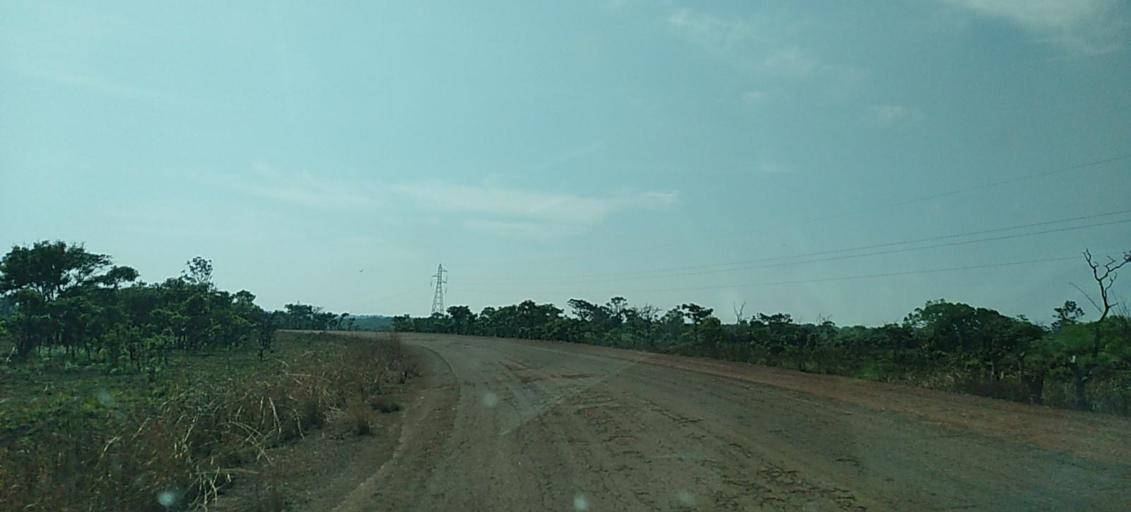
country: ZM
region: North-Western
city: Mwinilunga
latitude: -11.7864
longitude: 25.0279
